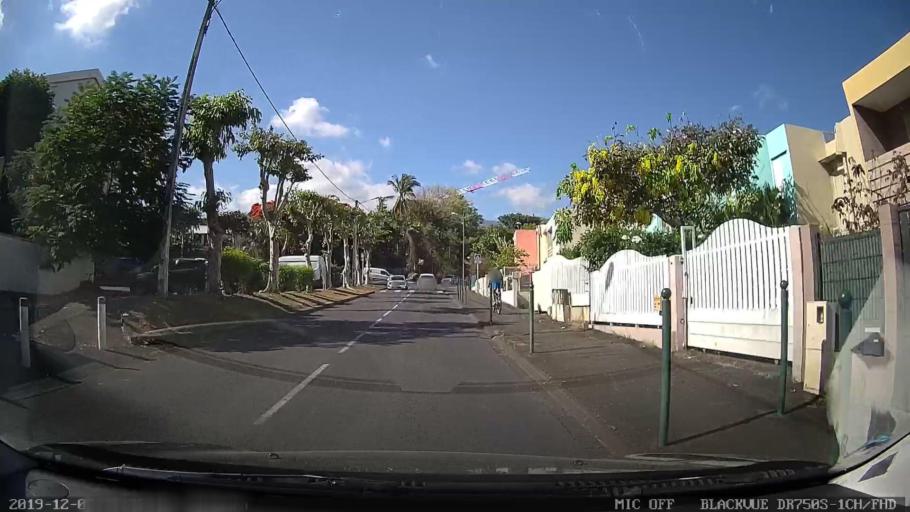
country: RE
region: Reunion
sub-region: Reunion
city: Saint-Denis
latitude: -20.8980
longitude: 55.4804
